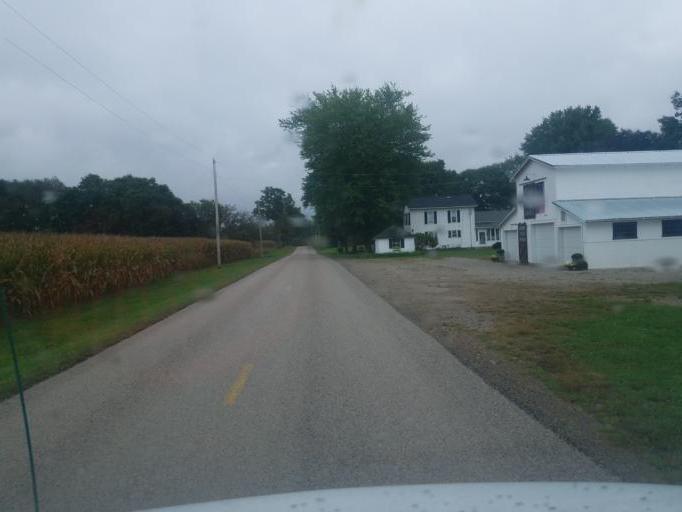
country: US
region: Ohio
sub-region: Ashland County
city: Ashland
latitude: 40.7937
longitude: -82.2043
